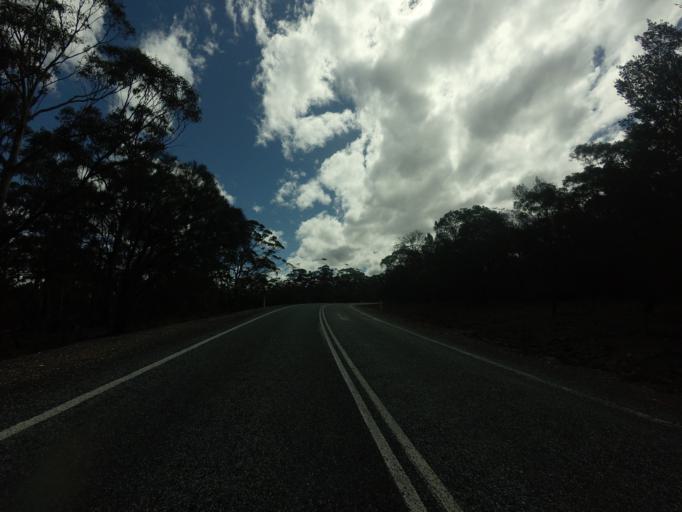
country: AU
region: Tasmania
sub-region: Break O'Day
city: St Helens
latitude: -42.0164
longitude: 148.0021
